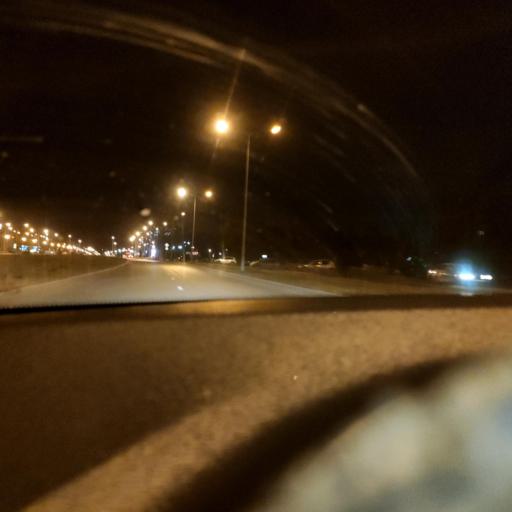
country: RU
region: Samara
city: Samara
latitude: 53.2584
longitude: 50.2439
